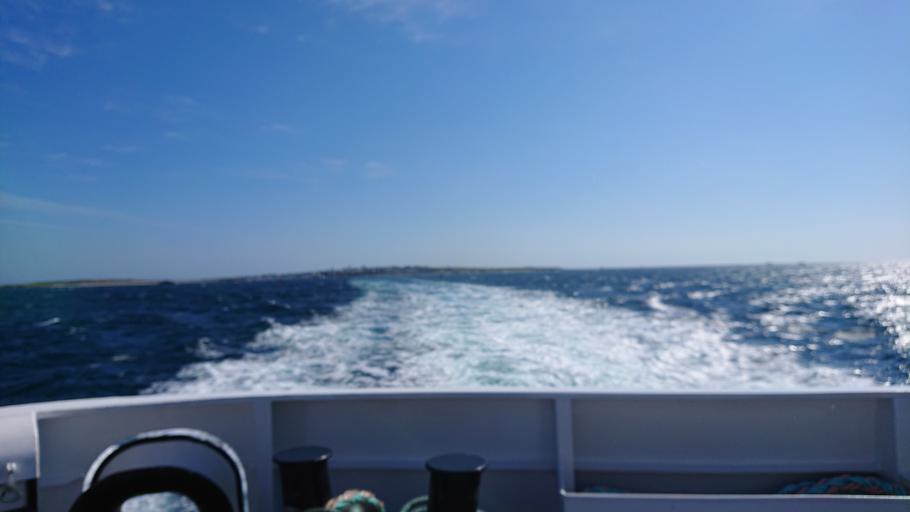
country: FR
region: Brittany
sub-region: Departement du Finistere
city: Le Conquet
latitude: 48.4136
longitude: -4.9490
